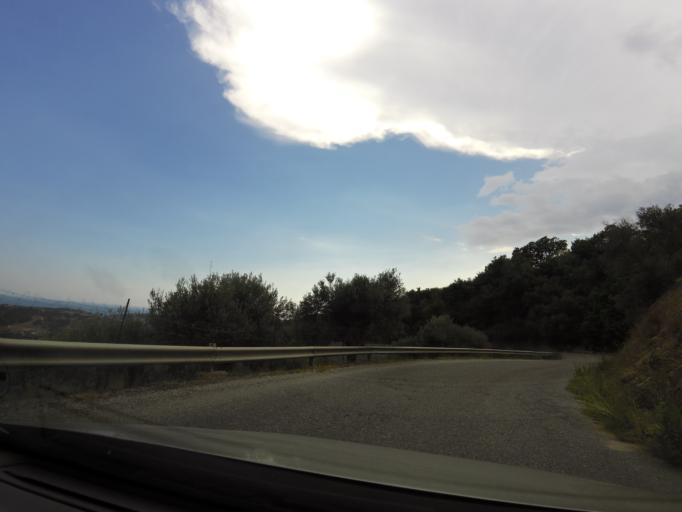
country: IT
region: Calabria
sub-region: Provincia di Reggio Calabria
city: Camini
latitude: 38.4373
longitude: 16.5148
